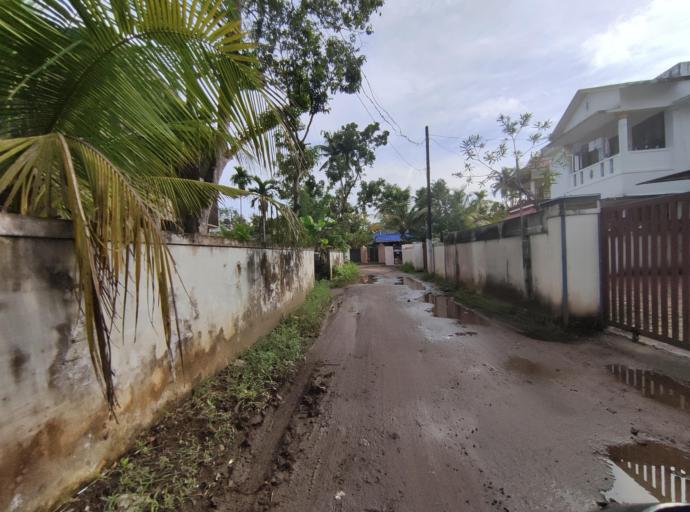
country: IN
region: Kerala
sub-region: Alappuzha
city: Vayalar
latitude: 9.6944
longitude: 76.3365
